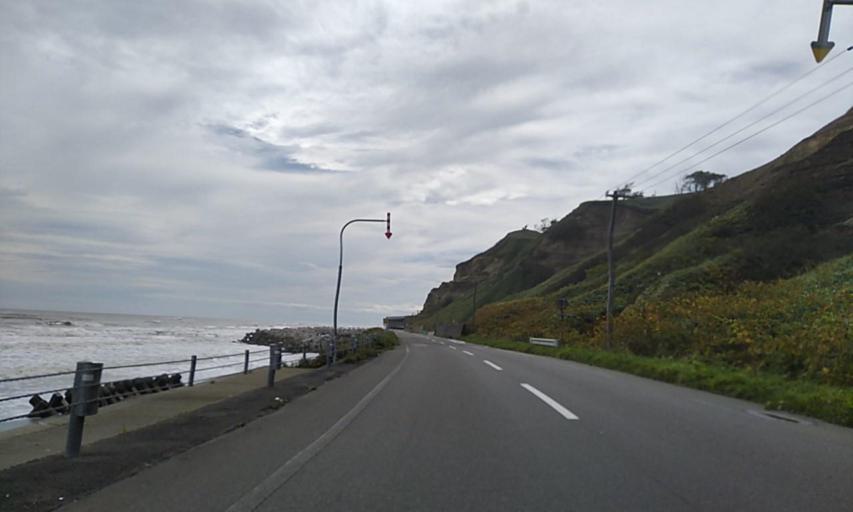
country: JP
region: Hokkaido
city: Obihiro
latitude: 42.7732
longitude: 143.7743
